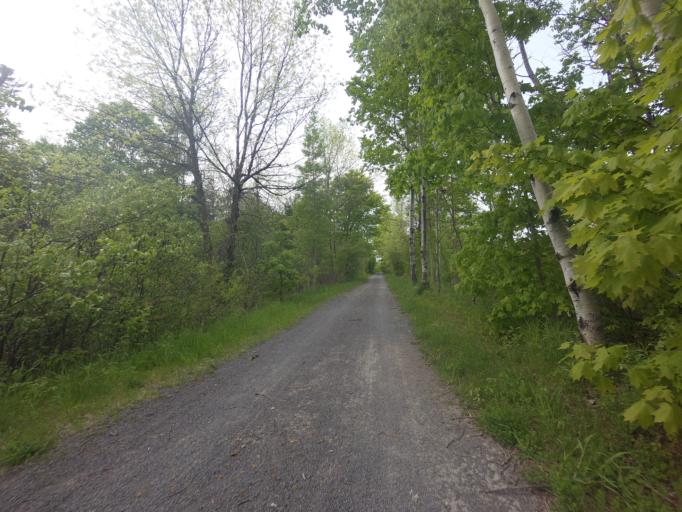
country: CA
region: Ontario
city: Kingston
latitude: 44.3076
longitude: -76.5822
